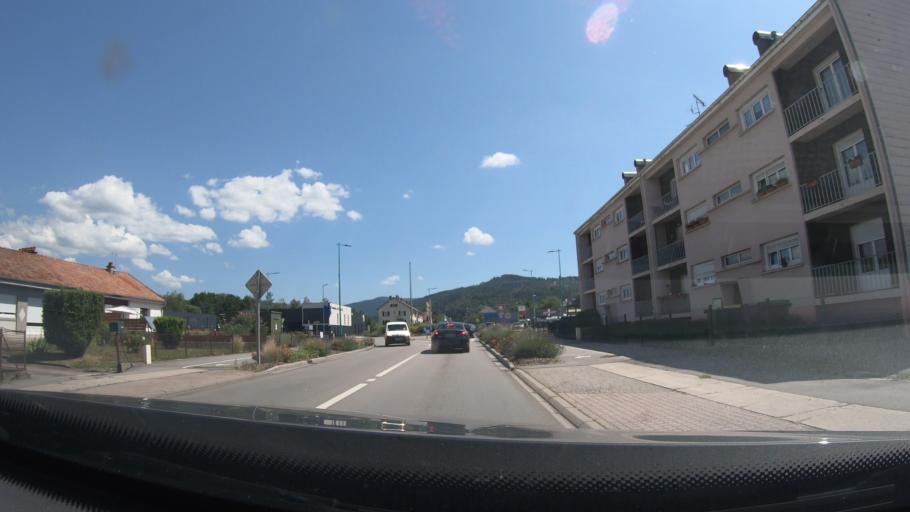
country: FR
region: Lorraine
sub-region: Departement des Vosges
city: Anould
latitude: 48.1942
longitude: 6.9495
